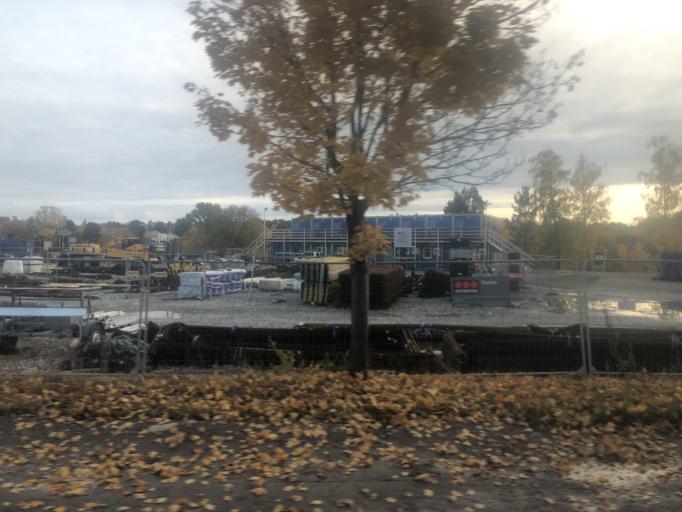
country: SE
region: Stockholm
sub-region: Jarfalla Kommun
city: Jakobsberg
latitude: 59.4050
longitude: 17.8587
